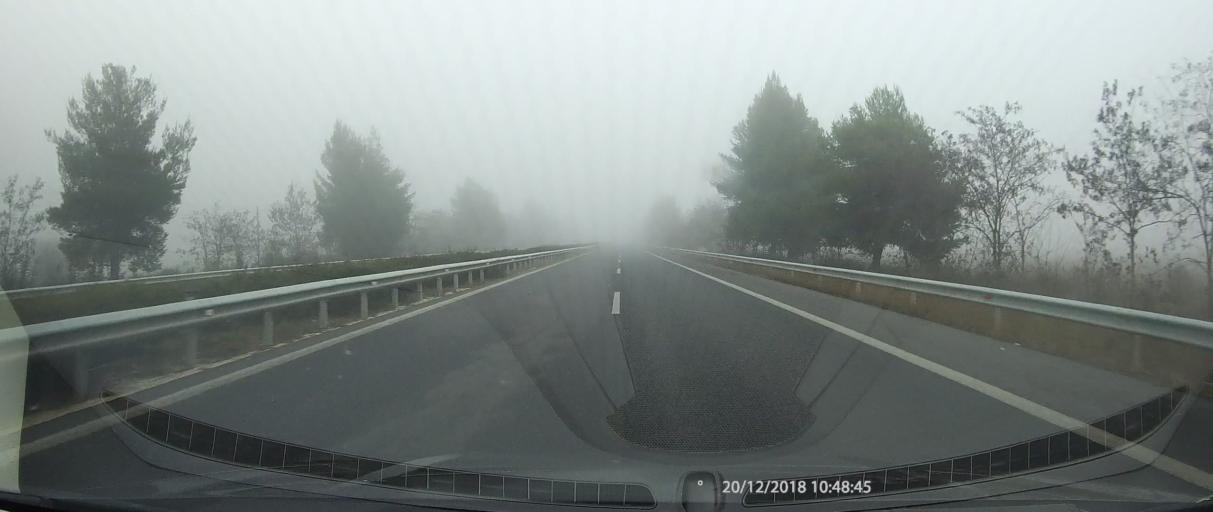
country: GR
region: Peloponnese
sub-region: Nomos Arkadias
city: Tripoli
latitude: 37.5235
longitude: 22.4084
